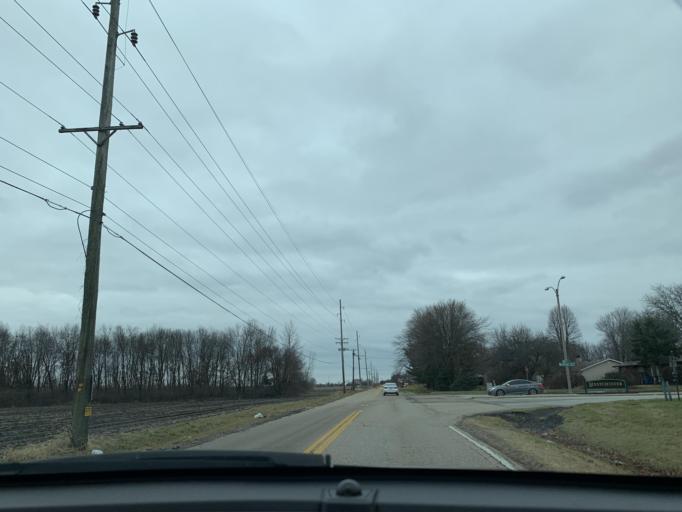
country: US
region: Illinois
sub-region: Sangamon County
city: Jerome
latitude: 39.7539
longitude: -89.6867
